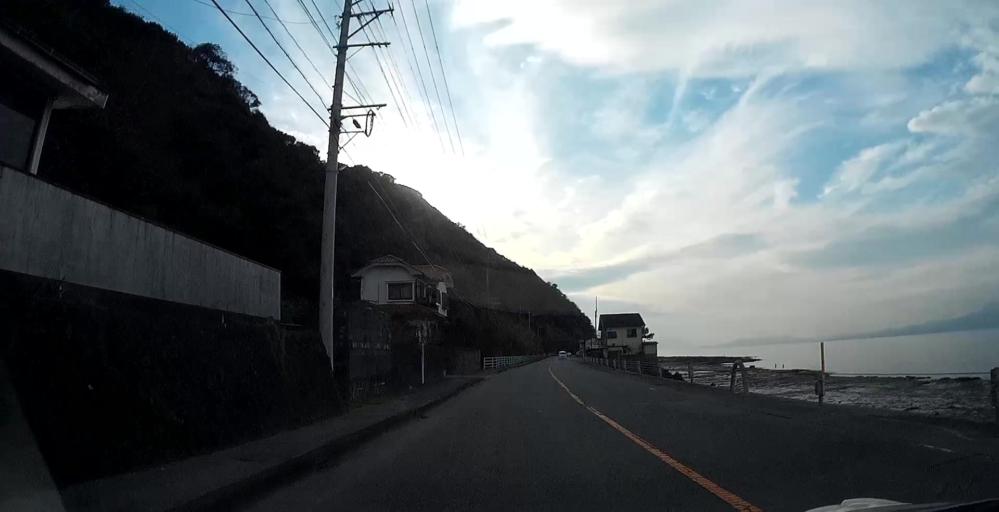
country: JP
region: Kumamoto
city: Matsubase
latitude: 32.6466
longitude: 130.4890
